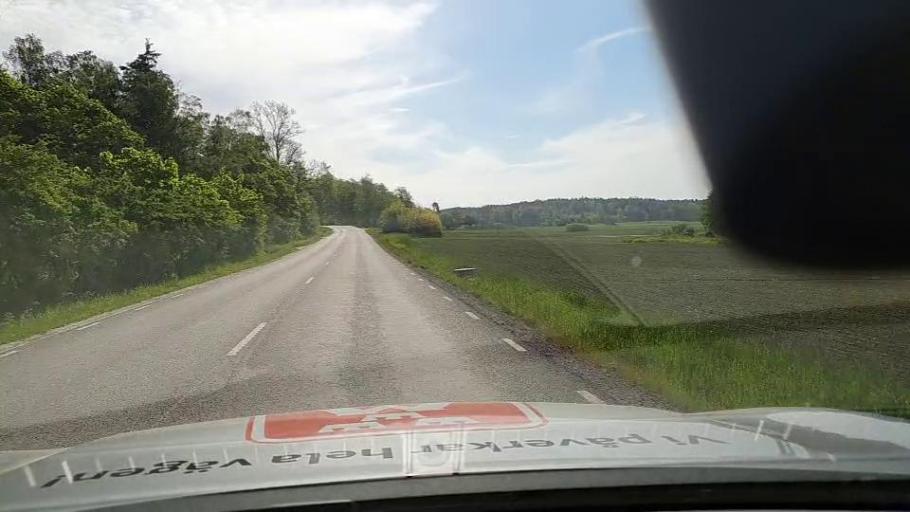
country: SE
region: Soedermanland
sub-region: Eskilstuna Kommun
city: Eskilstuna
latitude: 59.3179
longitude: 16.5822
